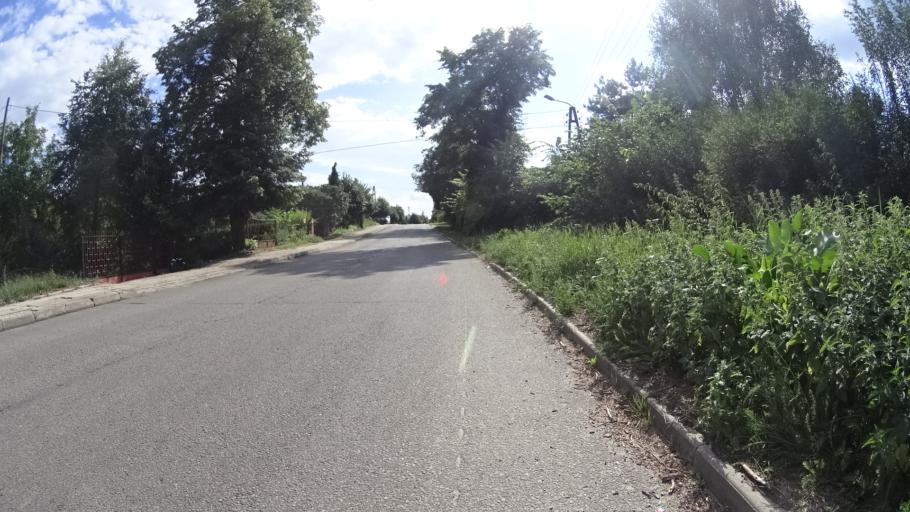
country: PL
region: Masovian Voivodeship
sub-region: Powiat grojecki
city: Mogielnica
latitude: 51.6879
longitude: 20.7195
